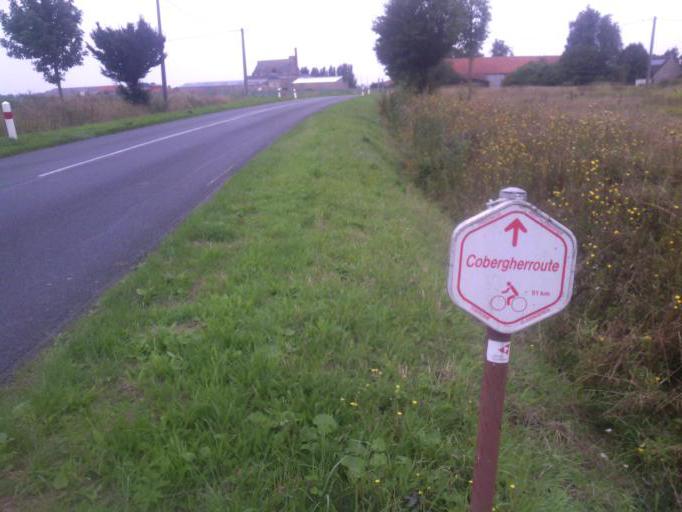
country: FR
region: Nord-Pas-de-Calais
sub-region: Departement du Nord
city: Killem
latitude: 50.9682
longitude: 2.5613
